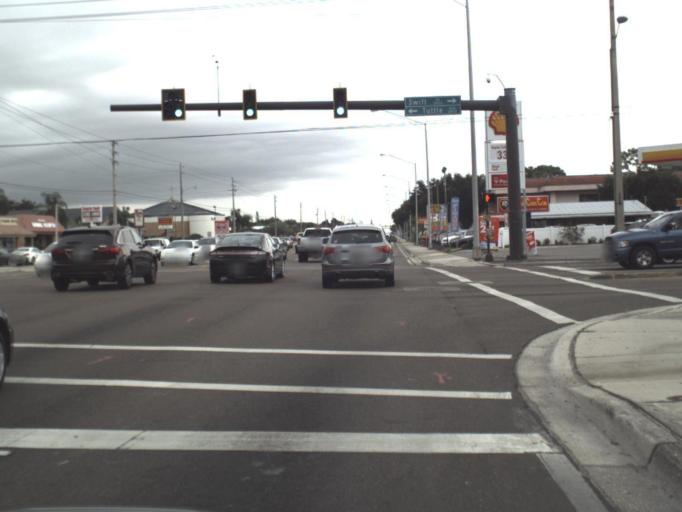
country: US
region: Florida
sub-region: Sarasota County
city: Southgate
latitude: 27.2987
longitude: -82.5145
